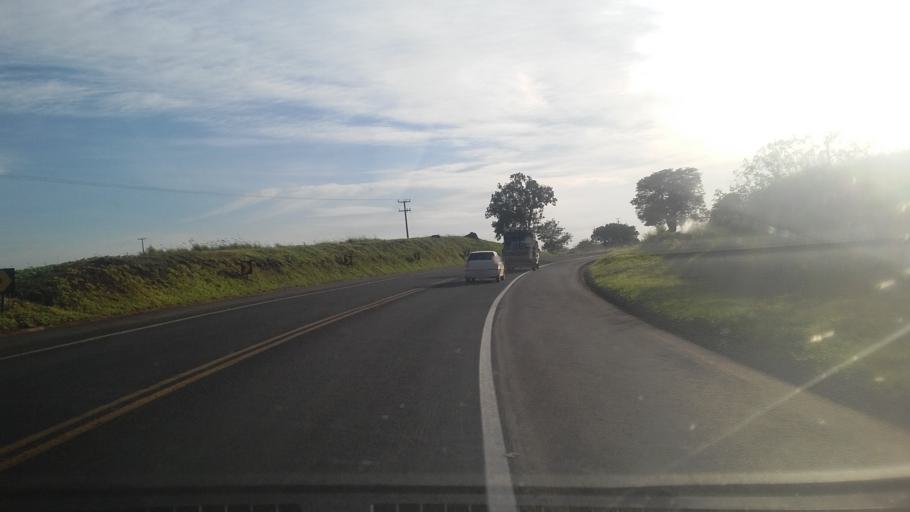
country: BR
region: Parana
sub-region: Bandeirantes
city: Bandeirantes
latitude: -23.1443
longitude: -50.5892
